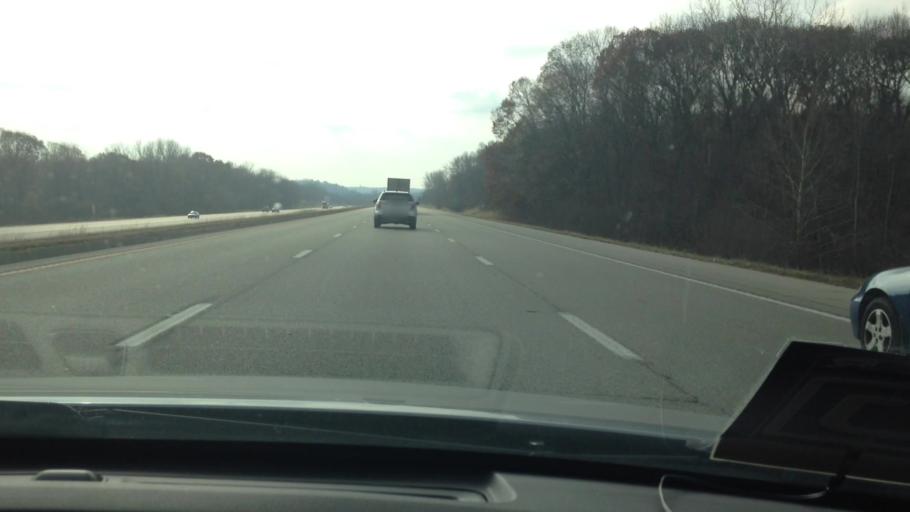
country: US
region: Missouri
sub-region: Platte County
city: Weatherby Lake
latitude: 39.2164
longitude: -94.7632
